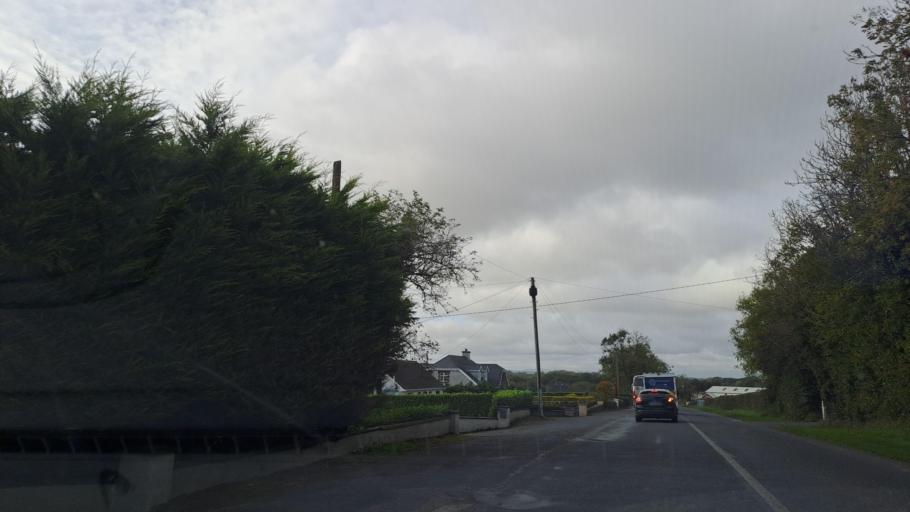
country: IE
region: Leinster
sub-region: An Mhi
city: Navan
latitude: 53.7276
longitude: -6.7060
